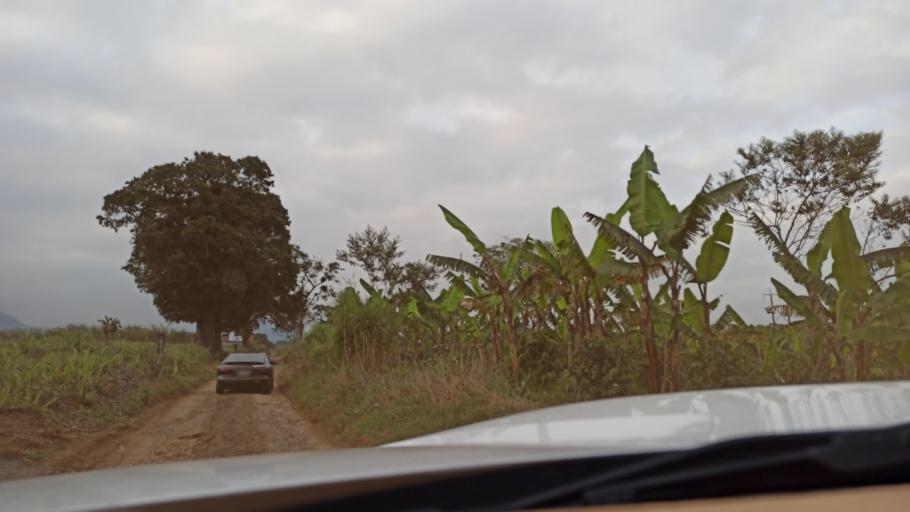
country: MX
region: Veracruz
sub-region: Fortin
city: Fraccionamiento Villas de la Llave
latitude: 18.9237
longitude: -97.0054
